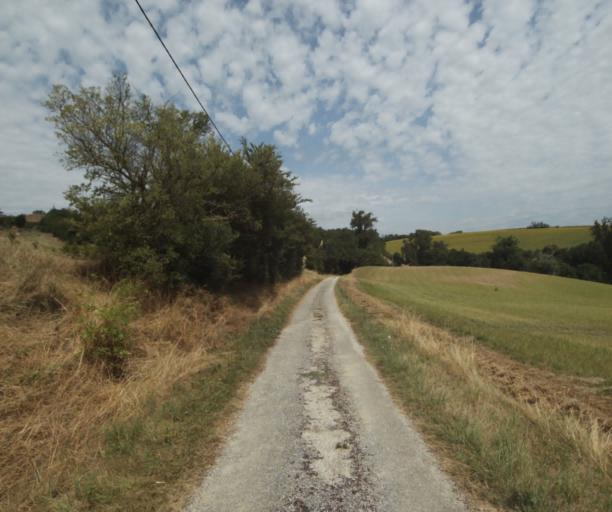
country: FR
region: Midi-Pyrenees
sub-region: Departement de la Haute-Garonne
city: Saint-Felix-Lauragais
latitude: 43.4448
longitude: 1.8917
